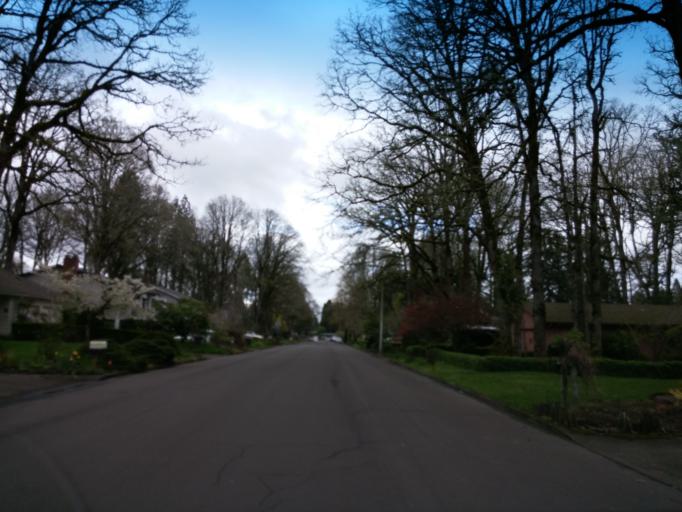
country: US
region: Oregon
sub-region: Washington County
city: Cedar Mill
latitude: 45.5331
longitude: -122.8187
